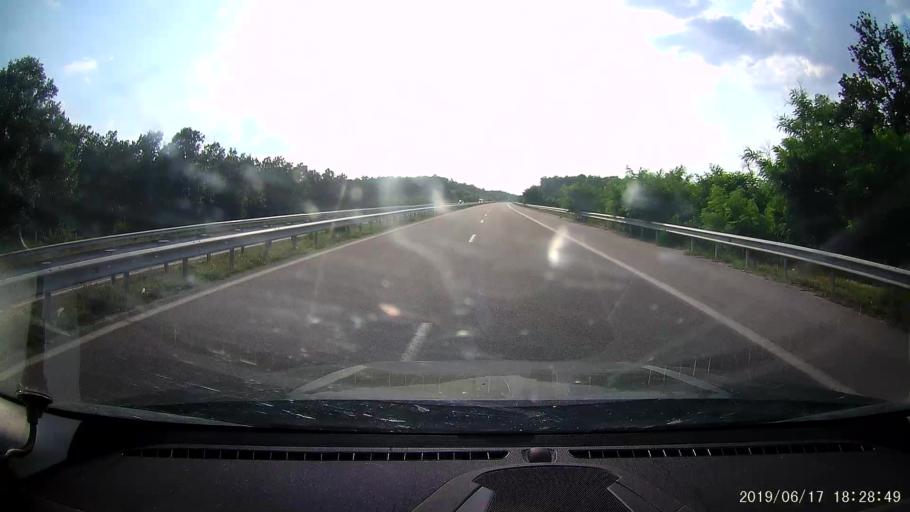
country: BG
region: Khaskovo
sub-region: Obshtina Dimitrovgrad
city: Dimitrovgrad
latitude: 42.0245
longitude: 25.5706
